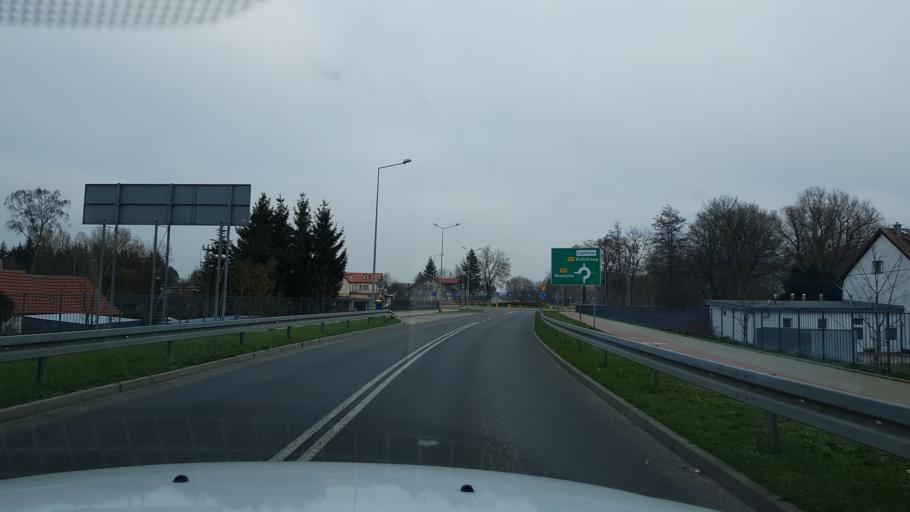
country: PL
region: West Pomeranian Voivodeship
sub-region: Powiat gryficki
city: Trzebiatow
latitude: 54.0639
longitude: 15.2608
